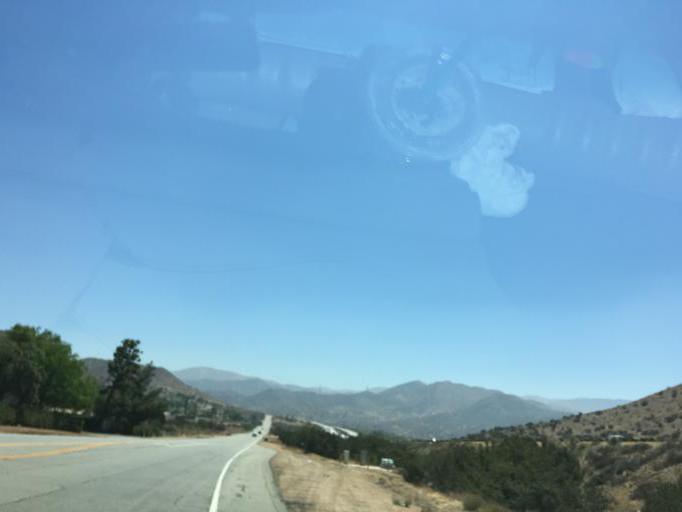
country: US
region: California
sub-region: Los Angeles County
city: Acton
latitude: 34.4936
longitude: -118.1708
